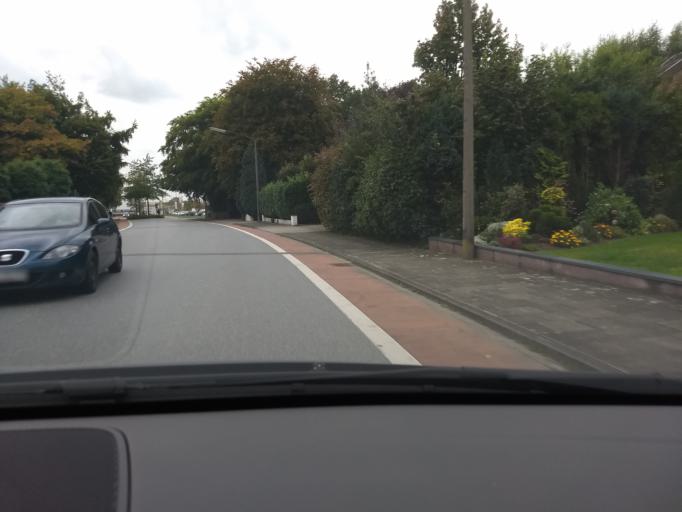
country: DE
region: North Rhine-Westphalia
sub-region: Regierungsbezirk Munster
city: Borken
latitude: 51.8468
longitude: 6.8753
